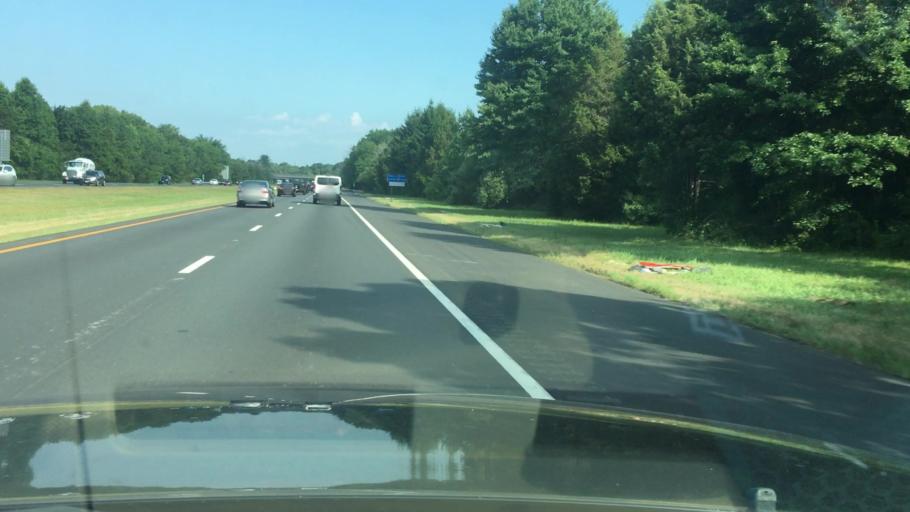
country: US
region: New Jersey
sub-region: Monmouth County
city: Shrewsbury
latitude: 40.1666
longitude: -74.4398
